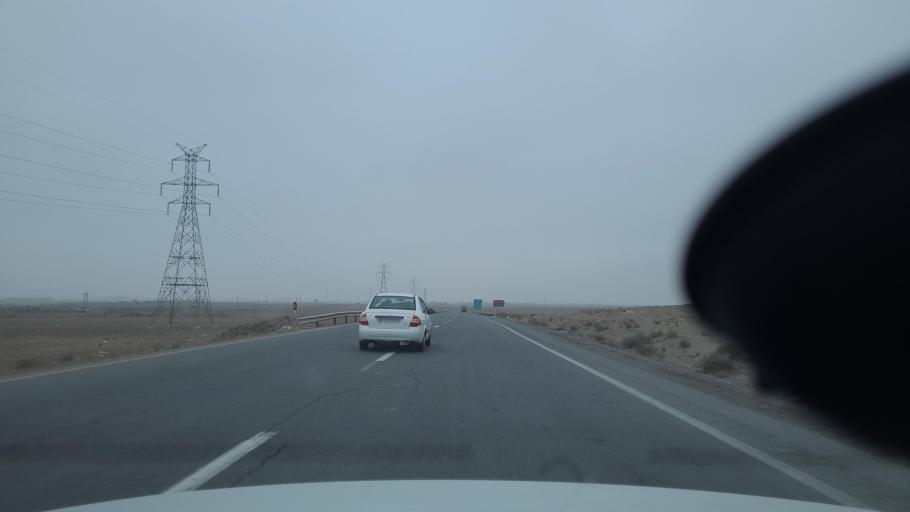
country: IR
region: Razavi Khorasan
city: Fariman
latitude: 35.9736
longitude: 59.7476
